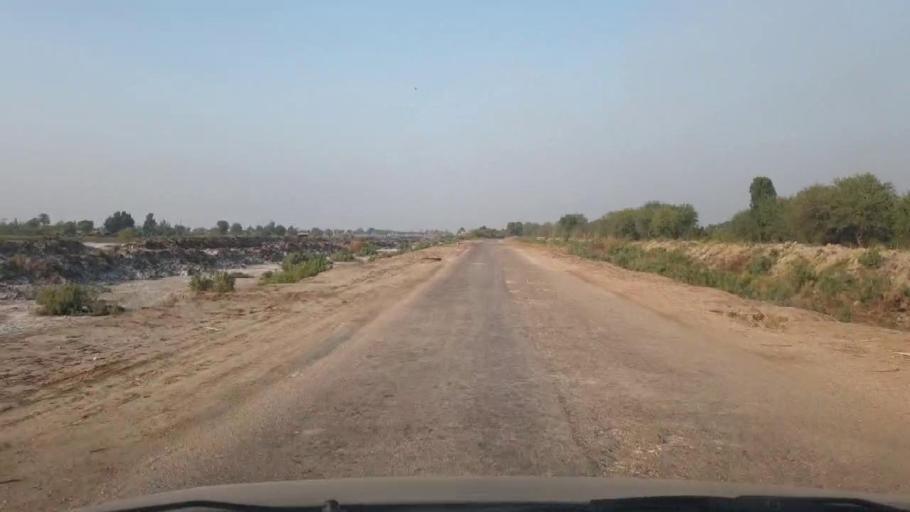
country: PK
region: Sindh
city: Mirwah Gorchani
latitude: 25.3632
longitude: 69.1764
